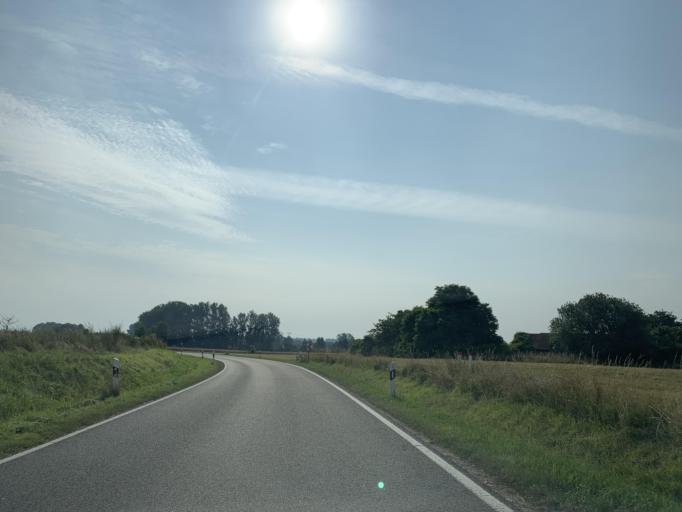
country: DE
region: Mecklenburg-Vorpommern
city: Blankensee
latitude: 53.4108
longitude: 13.2312
